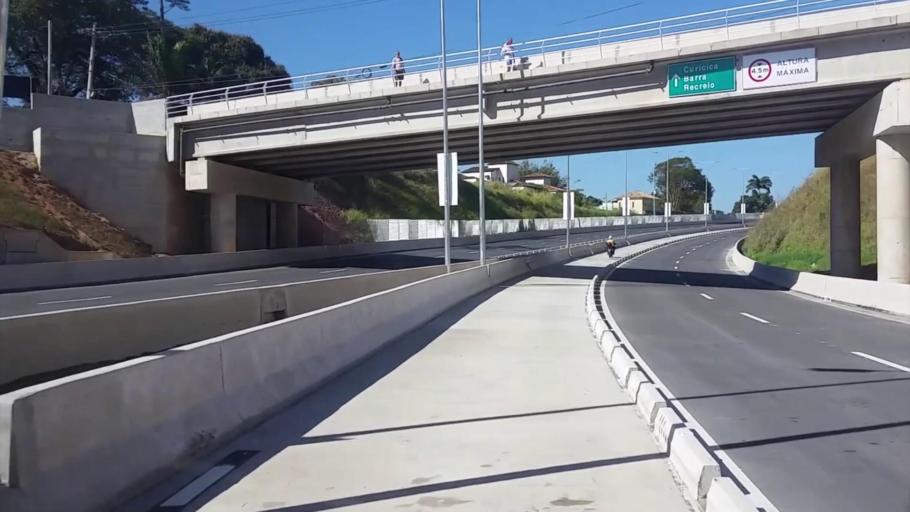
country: BR
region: Rio de Janeiro
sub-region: Nilopolis
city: Nilopolis
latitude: -22.9194
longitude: -43.3966
